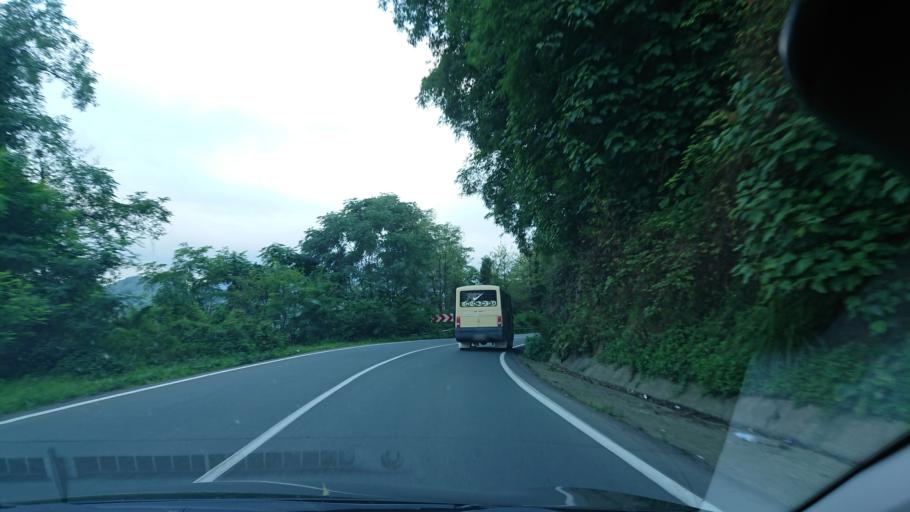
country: TR
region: Rize
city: Cayeli
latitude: 41.0747
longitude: 40.7114
